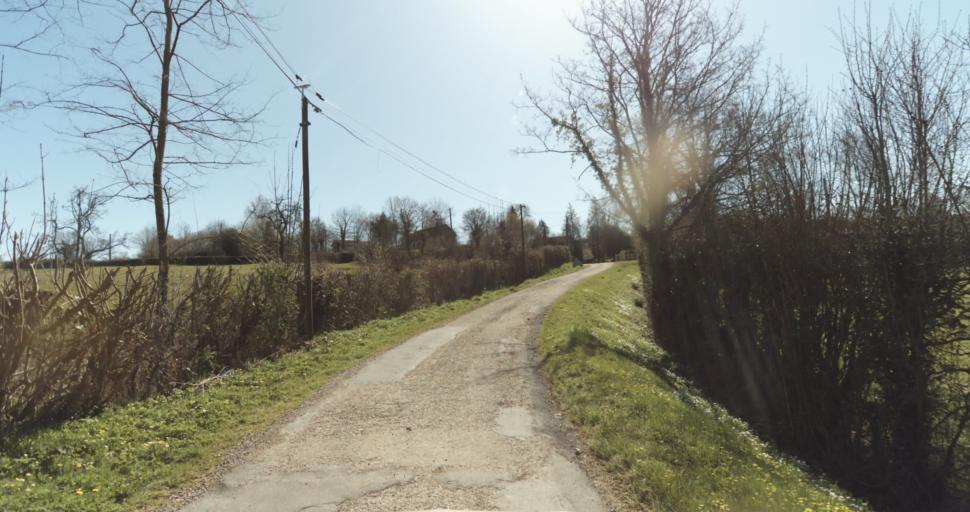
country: FR
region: Lower Normandy
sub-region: Departement du Calvados
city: Livarot
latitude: 48.9964
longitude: 0.0995
